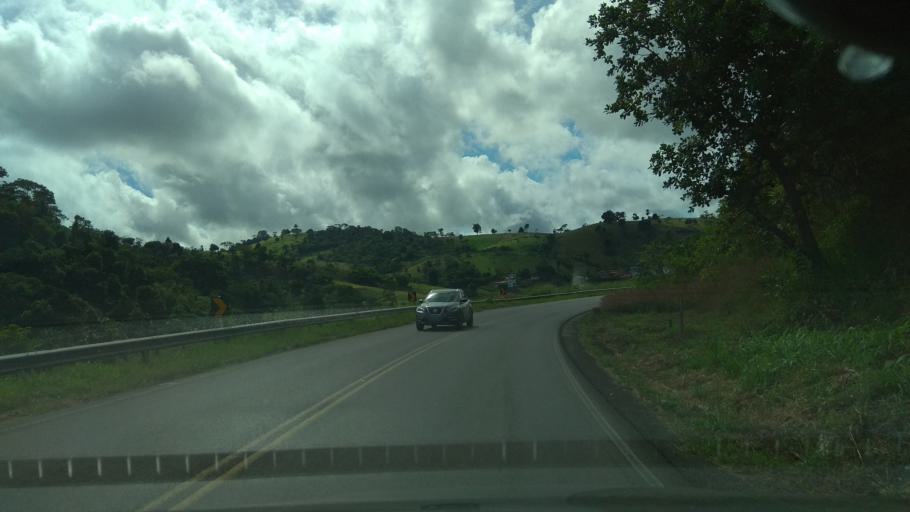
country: BR
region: Bahia
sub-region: Mutuipe
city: Mutuipe
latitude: -13.1834
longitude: -39.4393
